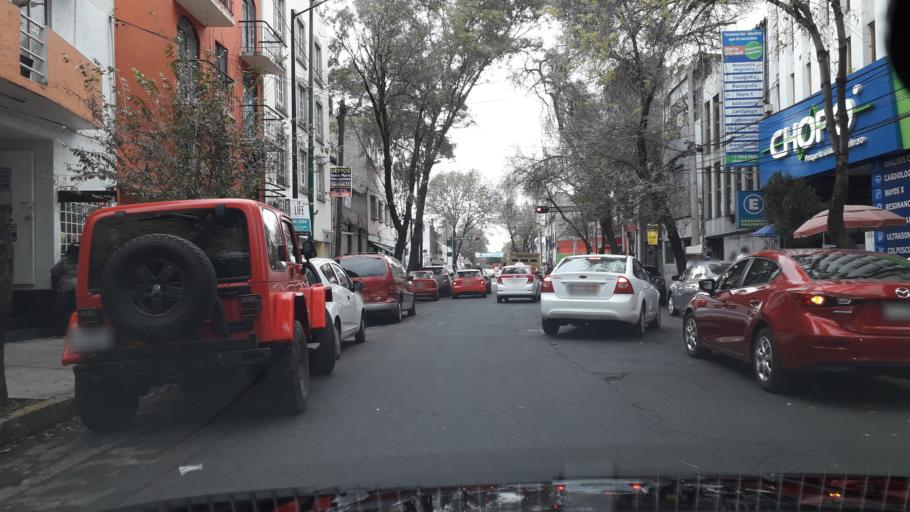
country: MX
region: Mexico City
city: Cuauhtemoc
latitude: 19.4461
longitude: -99.1557
